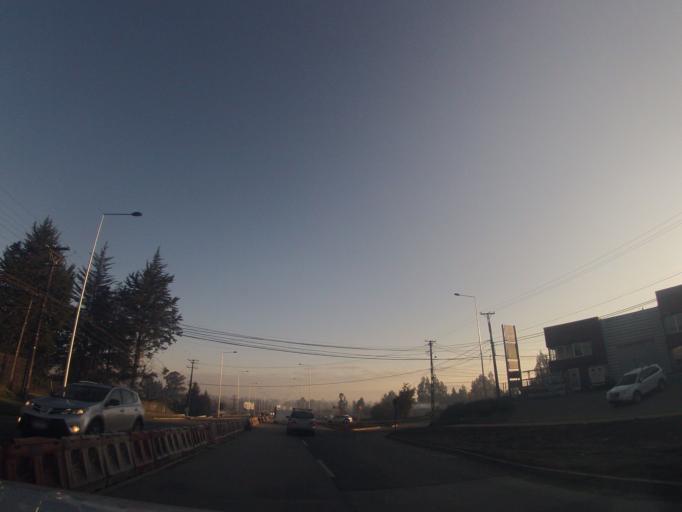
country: CL
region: Araucania
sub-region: Provincia de Cautin
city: Temuco
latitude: -38.7623
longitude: -72.6094
